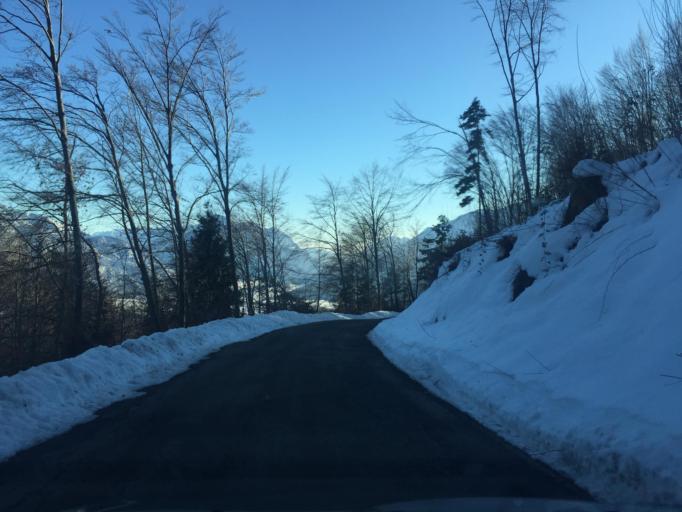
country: IT
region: Friuli Venezia Giulia
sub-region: Provincia di Udine
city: Chiaulis
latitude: 46.4241
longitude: 12.9866
